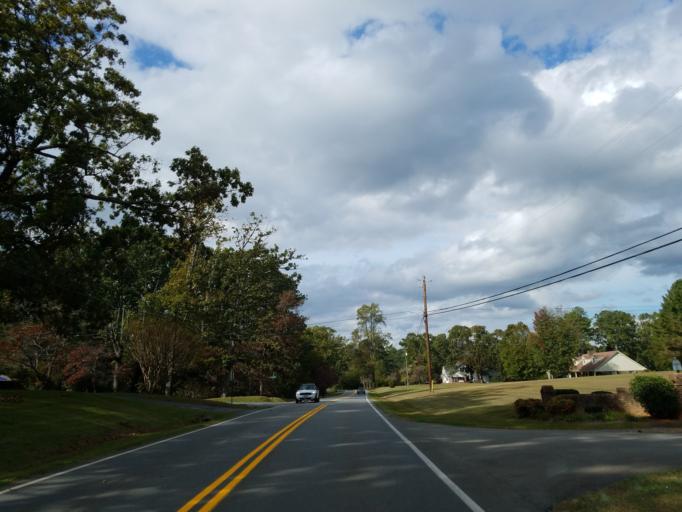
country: US
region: Georgia
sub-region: Pickens County
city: Jasper
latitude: 34.4505
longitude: -84.4239
